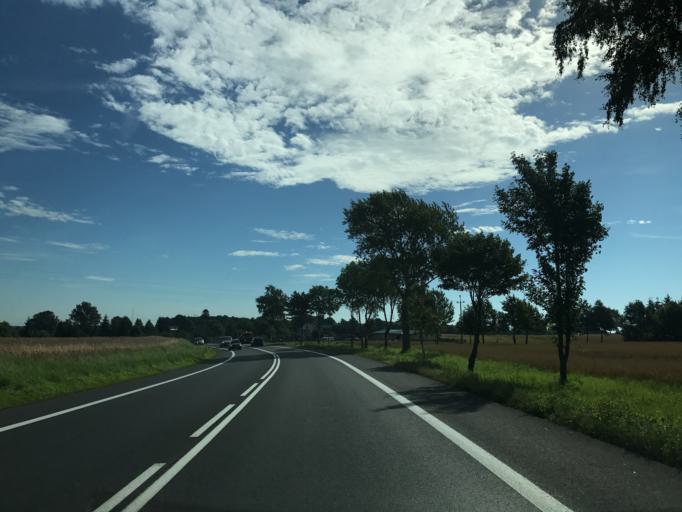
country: PL
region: West Pomeranian Voivodeship
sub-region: Powiat slawienski
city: Slawno
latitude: 54.3385
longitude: 16.6387
